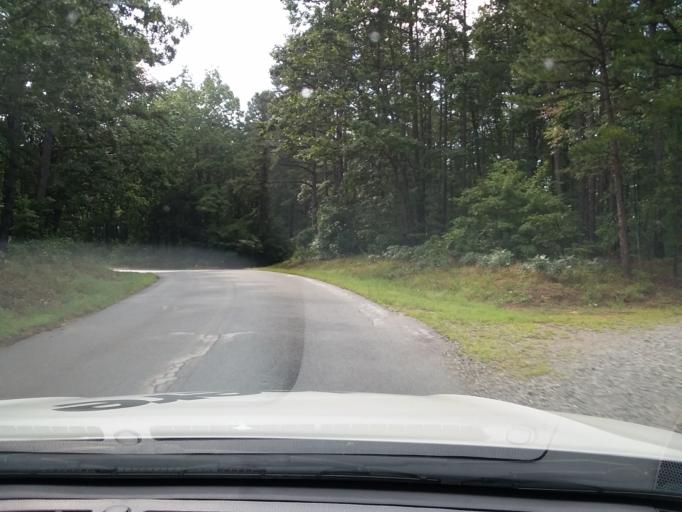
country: US
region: Georgia
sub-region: Habersham County
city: Clarkesville
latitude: 34.7133
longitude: -83.4105
